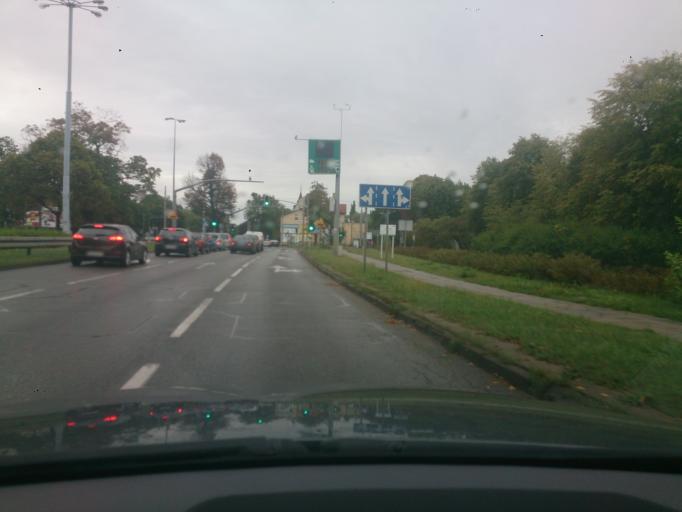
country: PL
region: Pomeranian Voivodeship
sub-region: Sopot
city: Sopot
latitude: 54.4151
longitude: 18.5660
